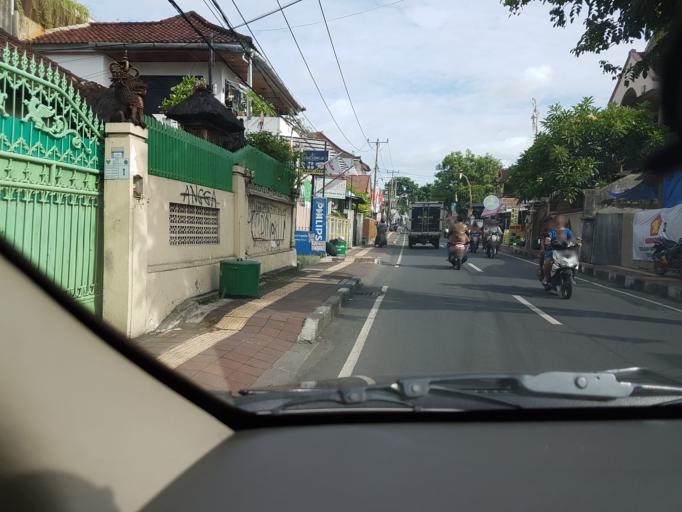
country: ID
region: Bali
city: Denpasar
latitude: -8.6615
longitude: 115.1986
